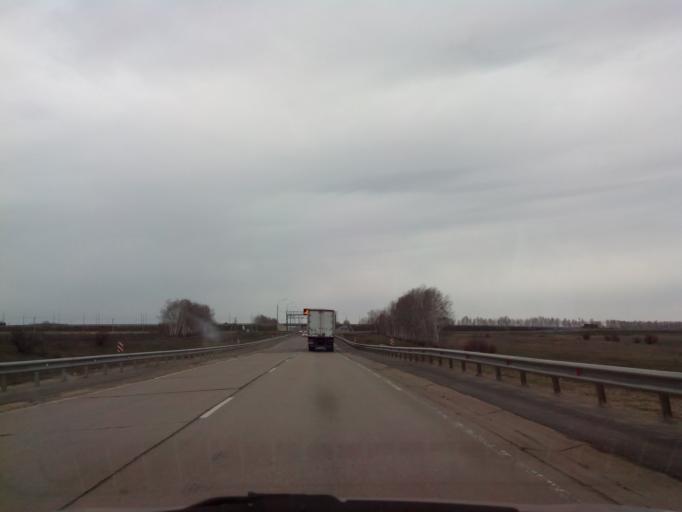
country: RU
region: Tambov
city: Pokrovo-Prigorodnoye
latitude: 52.6558
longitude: 41.3403
